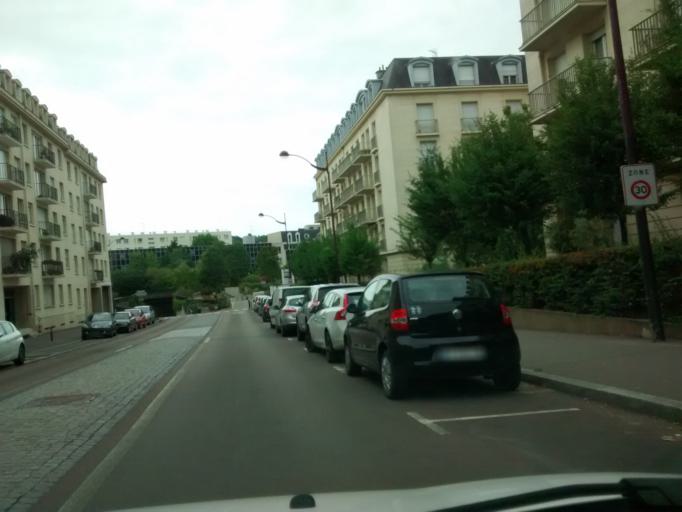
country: FR
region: Ile-de-France
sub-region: Departement des Yvelines
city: Versailles
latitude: 48.7979
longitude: 2.1436
